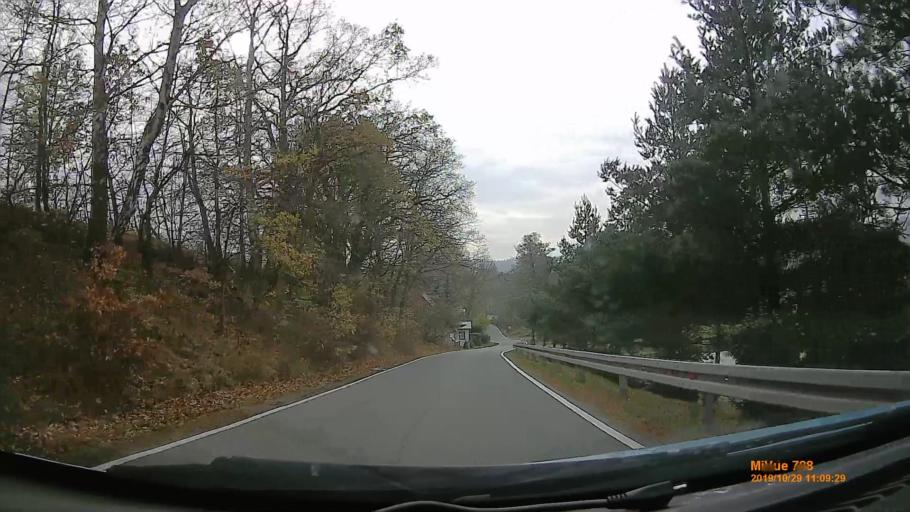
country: PL
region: Lower Silesian Voivodeship
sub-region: Powiat klodzki
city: Polanica-Zdroj
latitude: 50.4434
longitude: 16.4985
